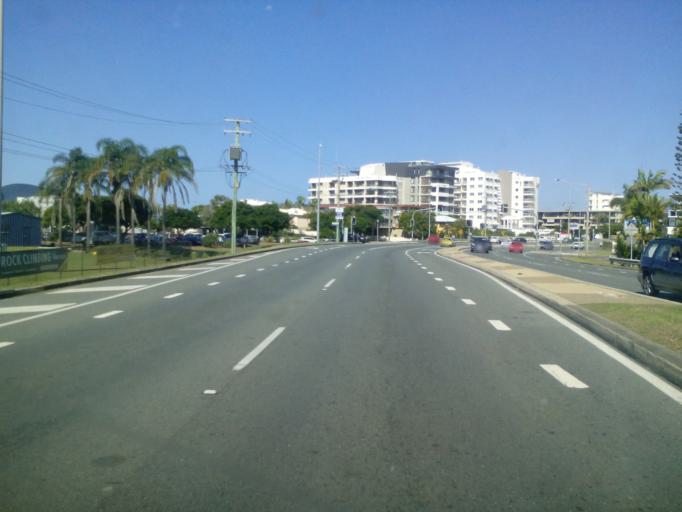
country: AU
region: Queensland
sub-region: Gold Coast
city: Palm Beach
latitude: -28.1001
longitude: 153.4606
